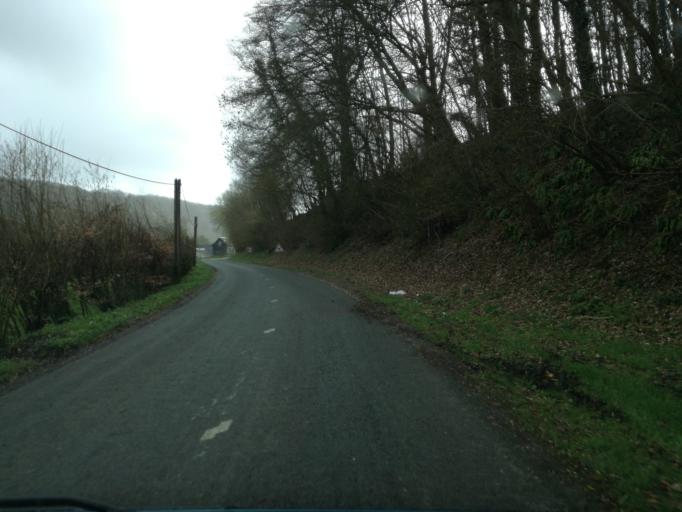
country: FR
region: Haute-Normandie
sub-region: Departement de la Seine-Maritime
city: Saint-Wandrille-Rancon
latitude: 49.5472
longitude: 0.7549
